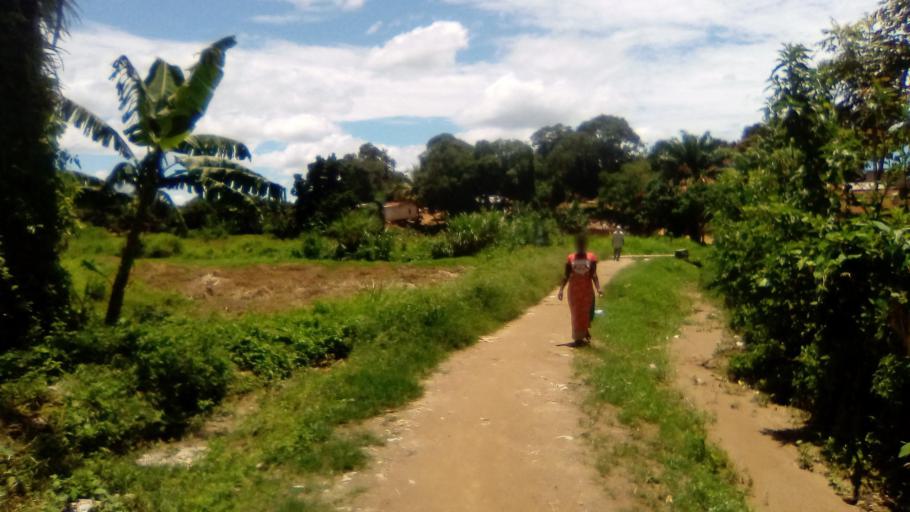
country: SL
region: Eastern Province
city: Simbakoro
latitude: 8.6228
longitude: -10.9907
